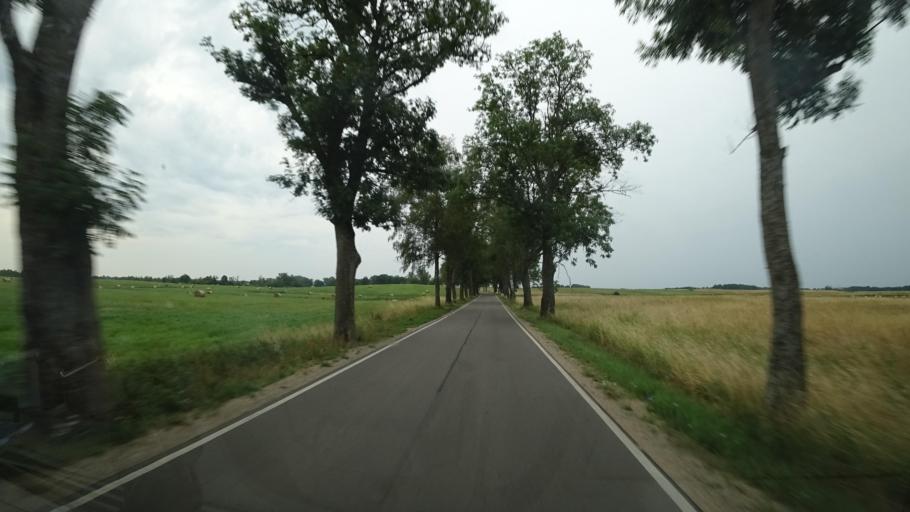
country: PL
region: Warmian-Masurian Voivodeship
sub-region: Powiat mragowski
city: Mikolajki
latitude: 53.8706
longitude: 21.5968
